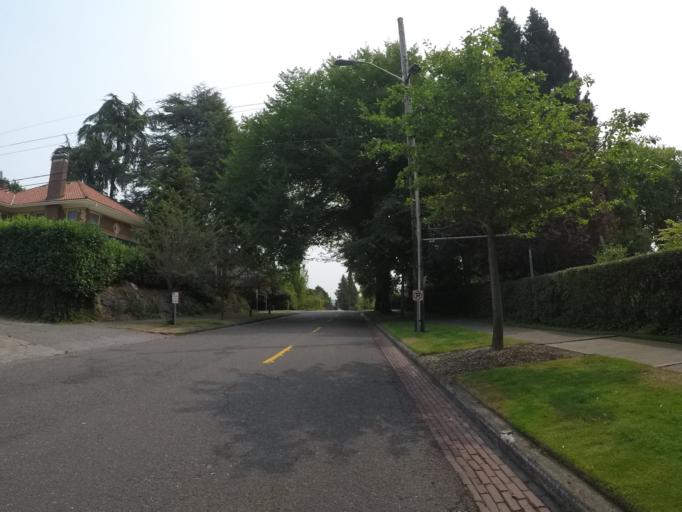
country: US
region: Washington
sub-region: King County
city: Seattle
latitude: 47.6268
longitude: -122.3043
